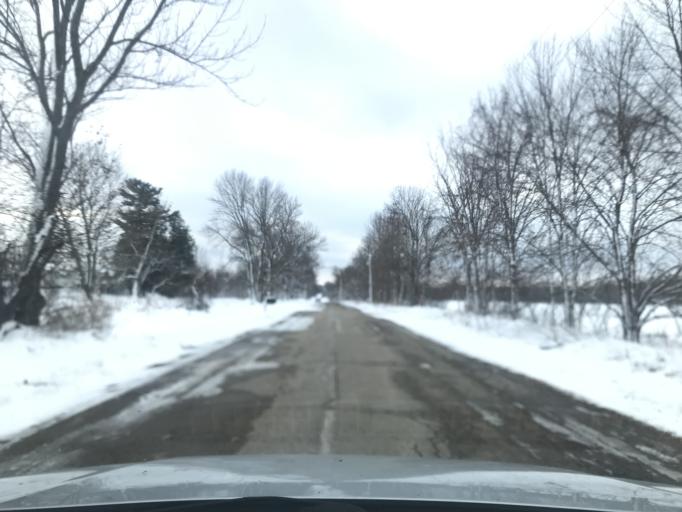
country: US
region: Wisconsin
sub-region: Oconto County
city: Oconto
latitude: 44.9209
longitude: -88.0001
